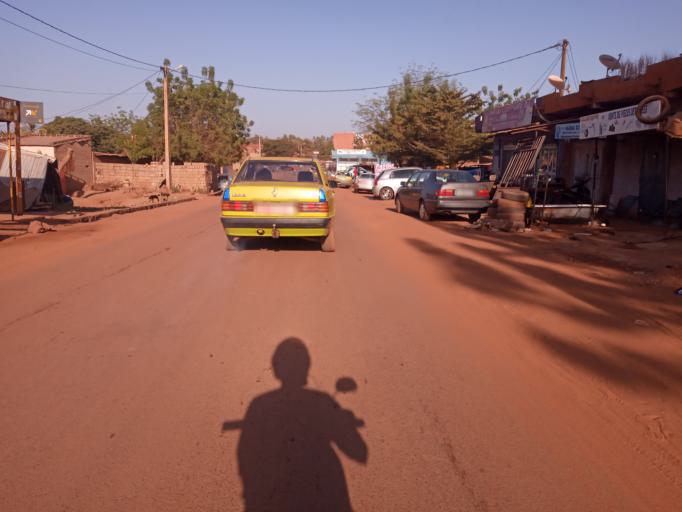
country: ML
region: Bamako
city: Bamako
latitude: 12.6139
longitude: -7.9506
